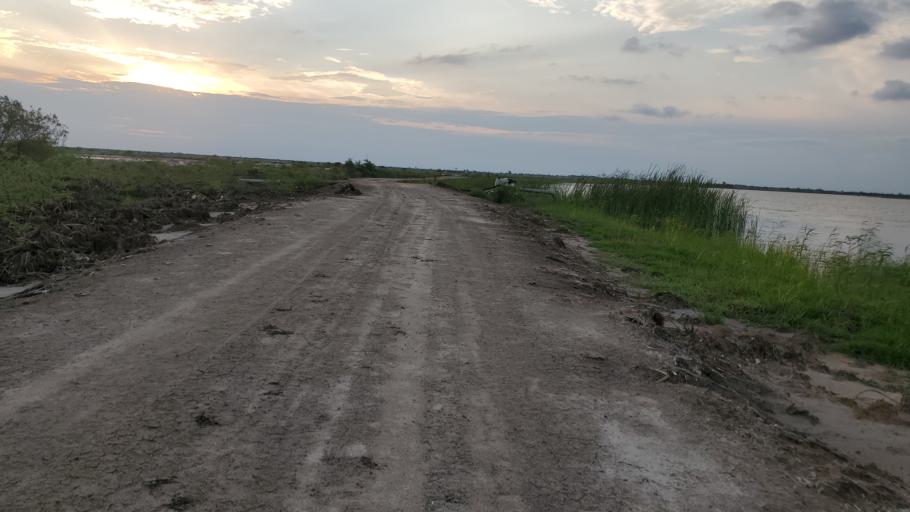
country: SN
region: Saint-Louis
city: Saint-Louis
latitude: 16.0186
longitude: -16.4040
